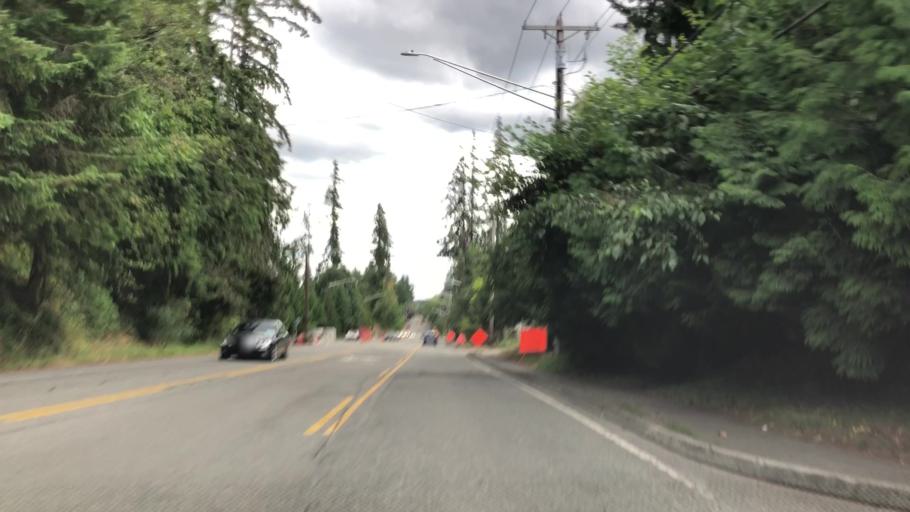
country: US
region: Washington
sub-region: Snohomish County
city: Alderwood Manor
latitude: 47.8401
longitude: -122.2818
